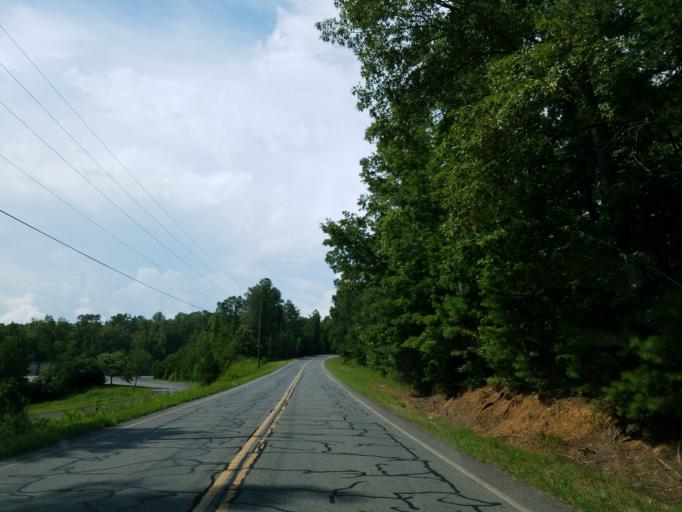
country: US
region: Georgia
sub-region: Gilmer County
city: Ellijay
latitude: 34.6061
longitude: -84.5946
